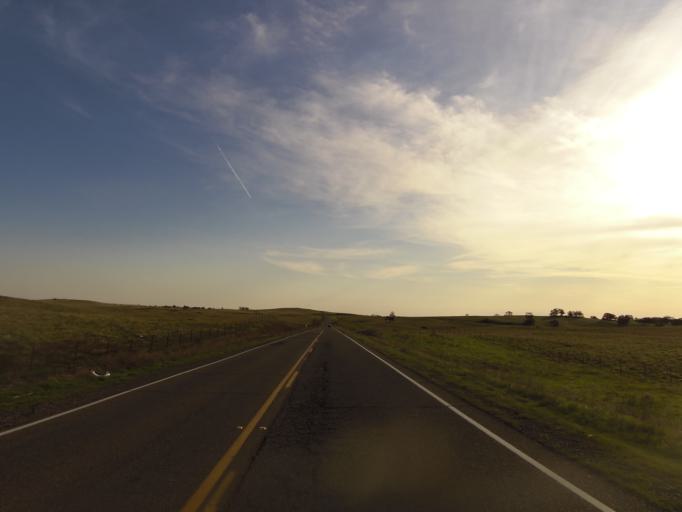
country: US
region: California
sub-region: El Dorado County
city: El Dorado Hills
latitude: 38.6336
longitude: -121.1142
